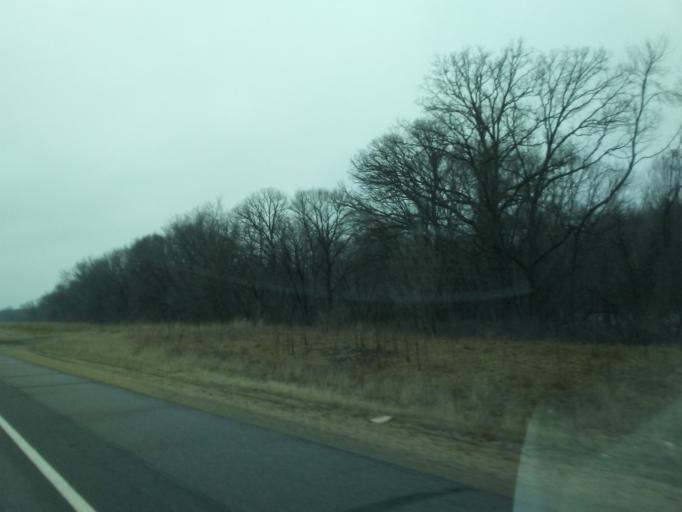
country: US
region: Wisconsin
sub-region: Sauk County
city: Spring Green
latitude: 43.1657
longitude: -90.0373
